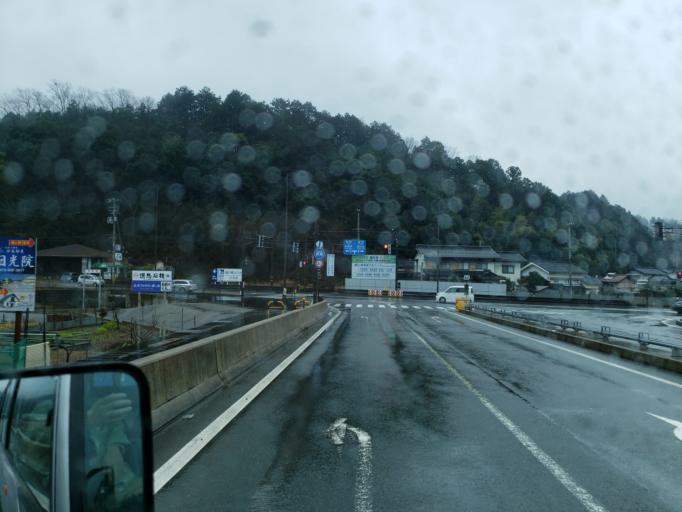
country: JP
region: Hyogo
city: Toyooka
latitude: 35.3928
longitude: 134.7510
